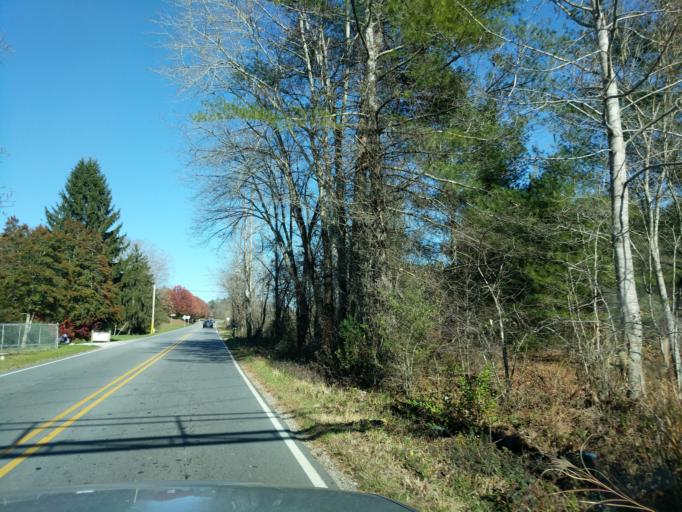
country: US
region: North Carolina
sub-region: Henderson County
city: Fletcher
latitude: 35.4404
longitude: -82.4917
